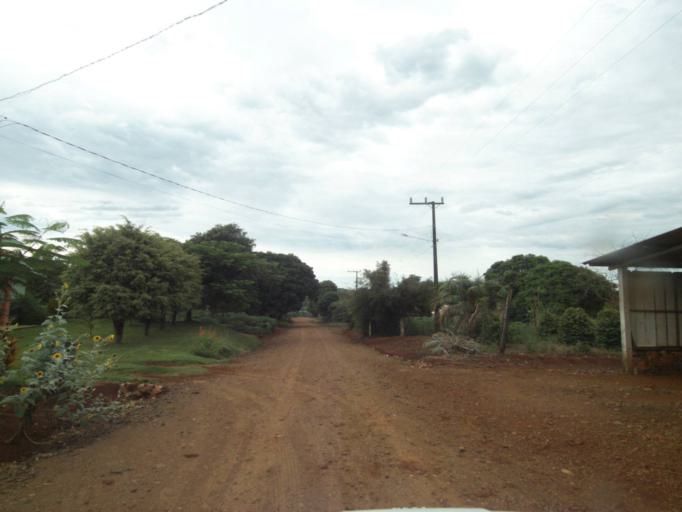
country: BR
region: Parana
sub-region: Guaraniacu
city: Guaraniacu
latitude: -24.9217
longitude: -52.9416
